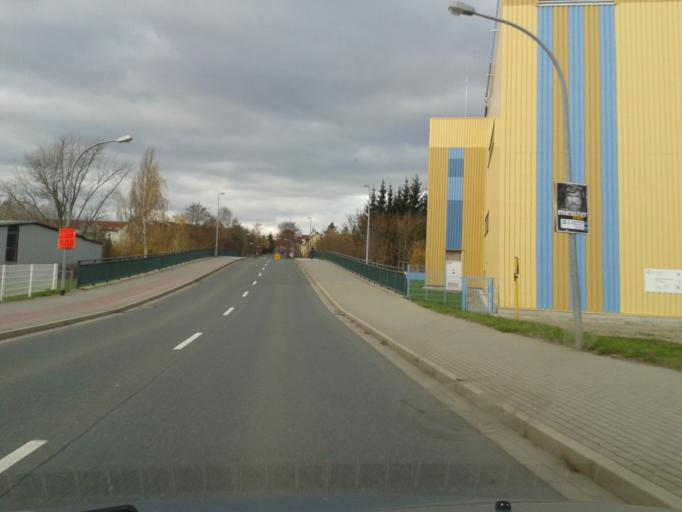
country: DE
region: Thuringia
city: Hermsdorf
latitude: 50.9003
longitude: 11.8522
